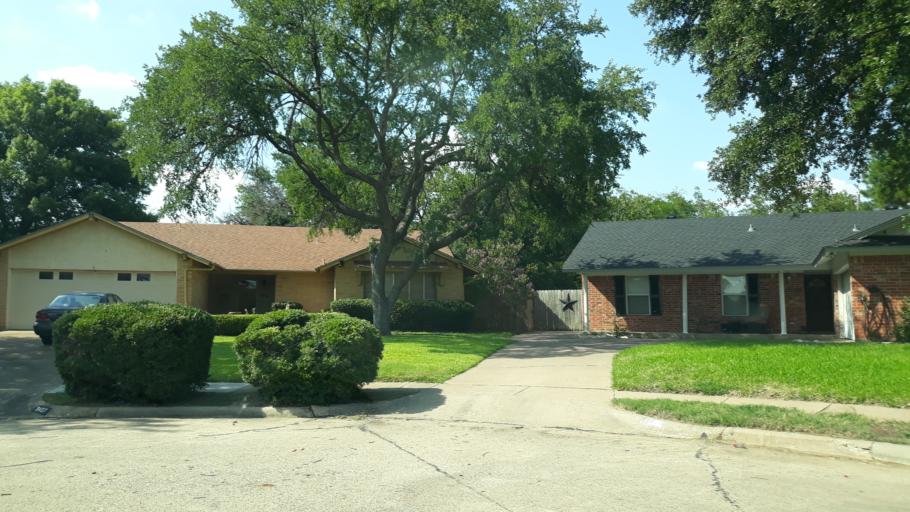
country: US
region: Texas
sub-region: Dallas County
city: Irving
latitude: 32.8455
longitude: -96.9945
